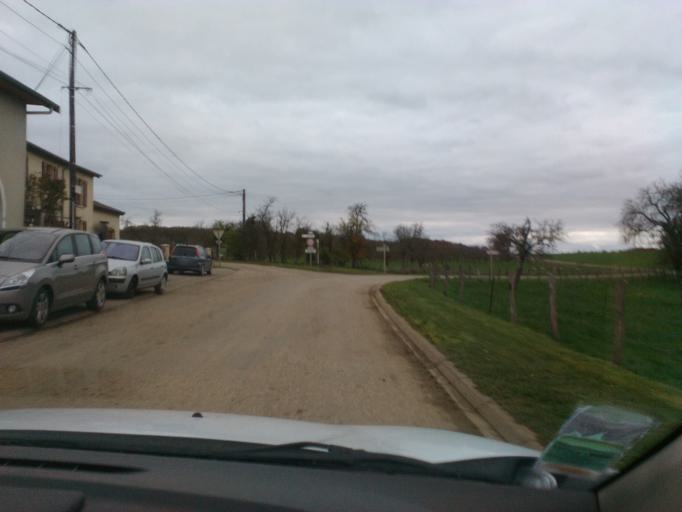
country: FR
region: Lorraine
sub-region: Departement des Vosges
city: Mirecourt
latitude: 48.2826
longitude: 6.1962
